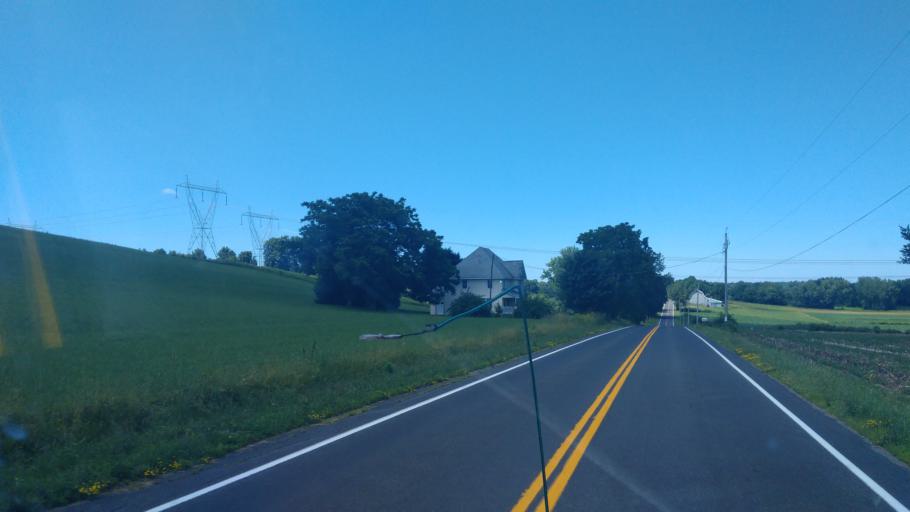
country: US
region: New York
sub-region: Wayne County
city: Lyons
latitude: 43.1286
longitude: -76.9584
